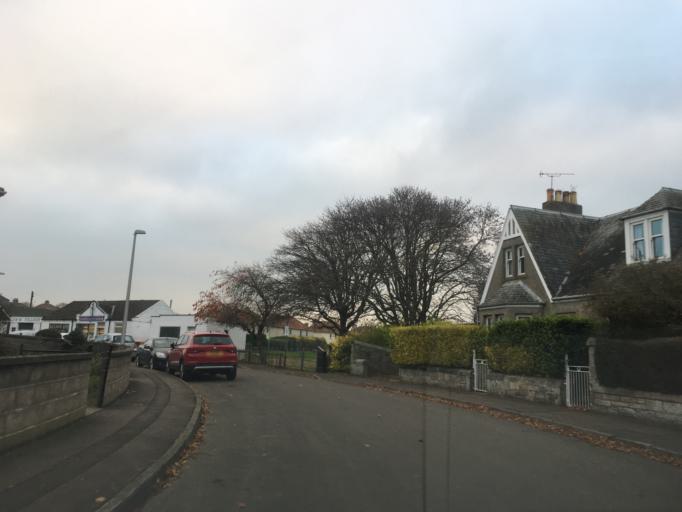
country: GB
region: Scotland
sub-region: Fife
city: Saint Andrews
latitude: 56.3354
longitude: -2.7851
